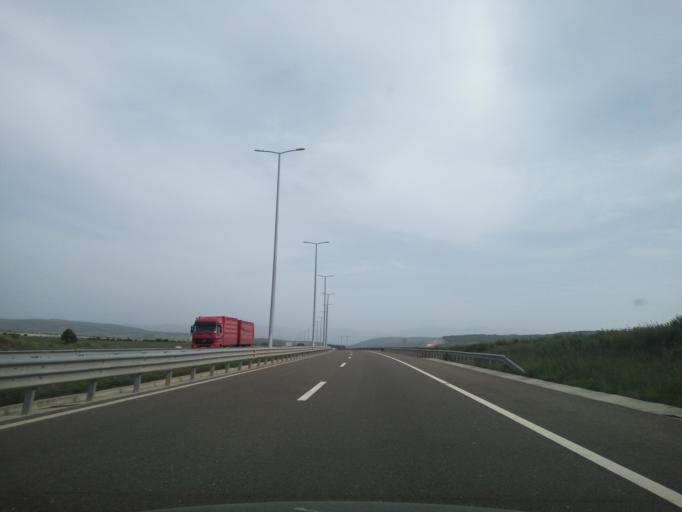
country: XK
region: Prizren
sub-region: Komuna e Malisheves
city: Malisevo
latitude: 42.4795
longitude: 20.7954
